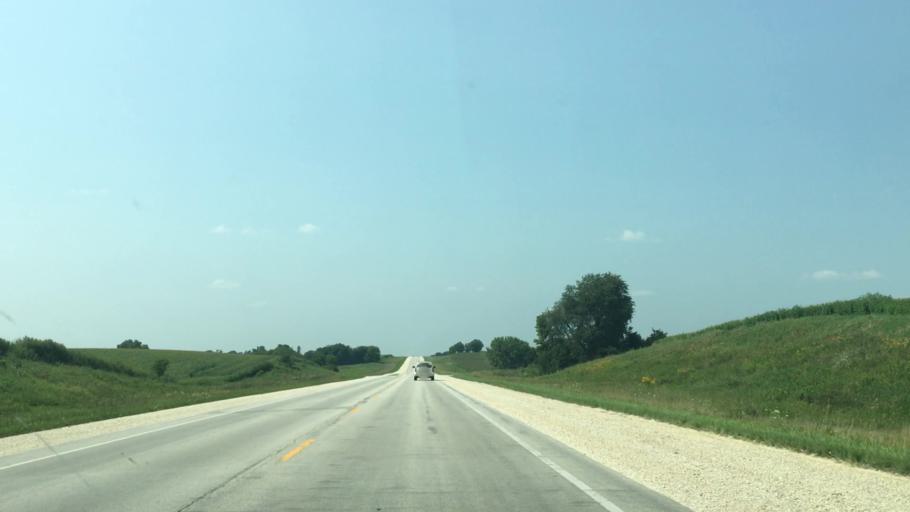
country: US
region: Iowa
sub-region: Winneshiek County
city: Decorah
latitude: 43.3749
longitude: -91.8139
